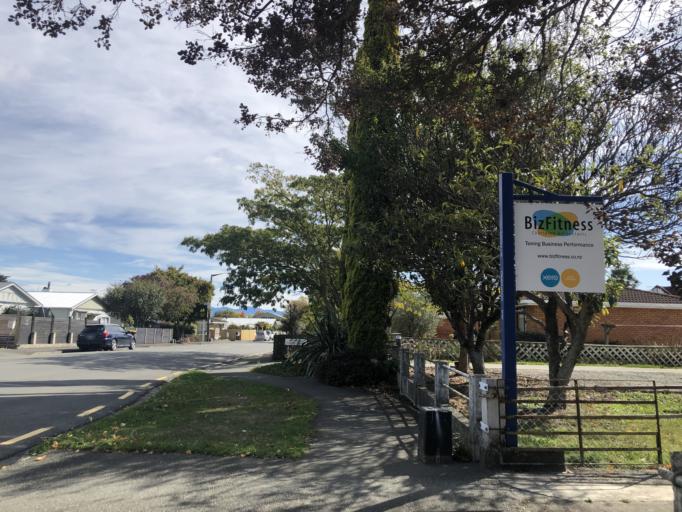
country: NZ
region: Tasman
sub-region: Tasman District
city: Richmond
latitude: -41.3405
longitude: 173.1839
